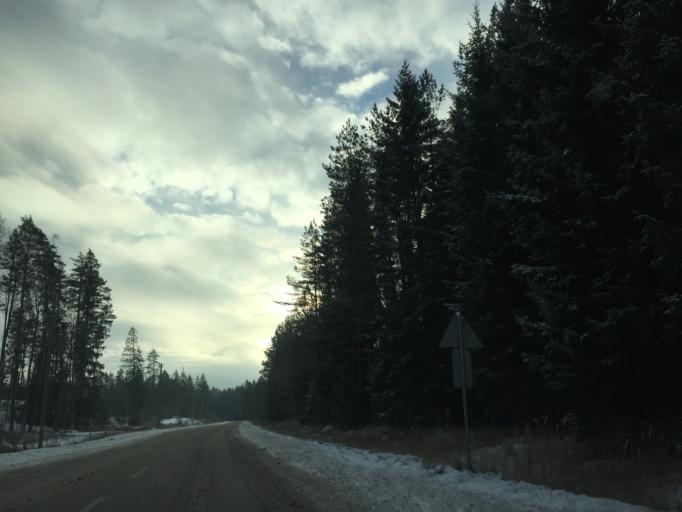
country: LV
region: Amatas Novads
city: Drabesi
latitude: 57.2249
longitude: 25.2829
